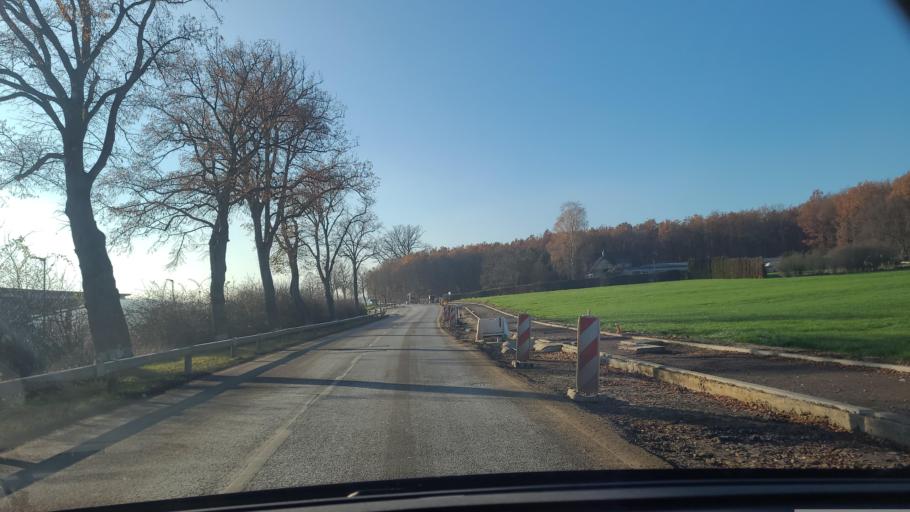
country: LU
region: Luxembourg
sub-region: Canton de Capellen
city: Mamer
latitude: 49.6210
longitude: 6.0060
